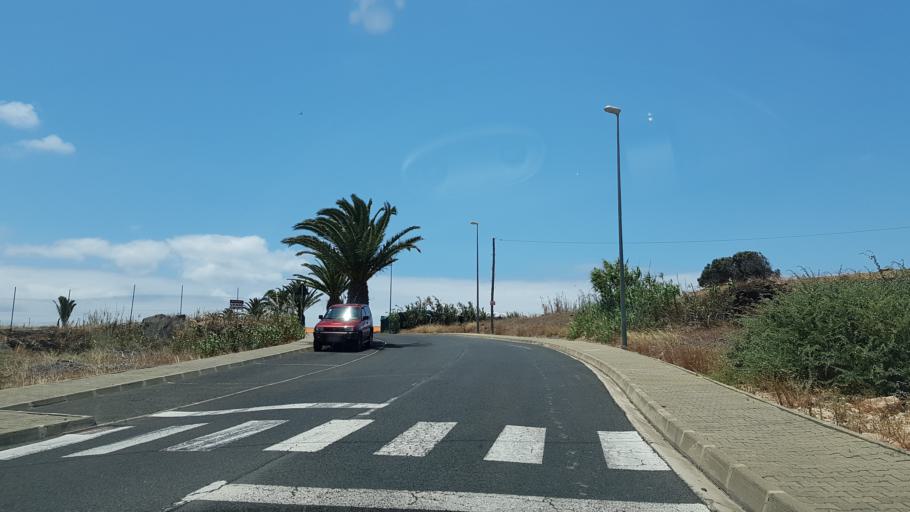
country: PT
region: Madeira
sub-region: Porto Santo
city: Vila de Porto Santo
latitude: 33.0669
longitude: -16.3433
